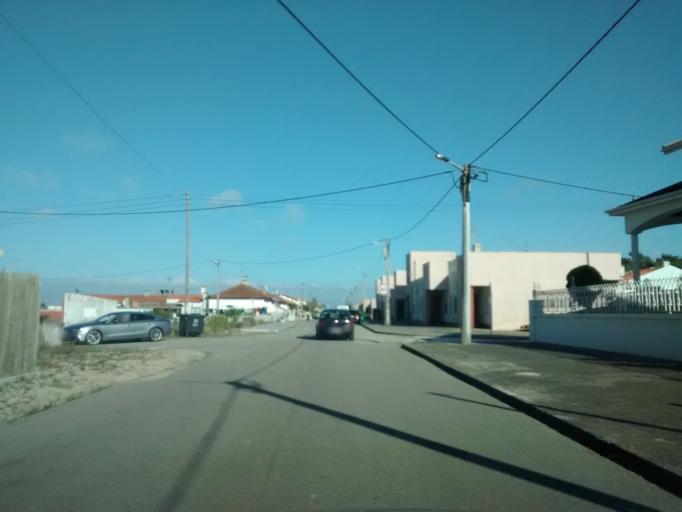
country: PT
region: Aveiro
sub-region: Ilhavo
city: Gafanha da Nazare
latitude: 40.6661
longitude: -8.7358
